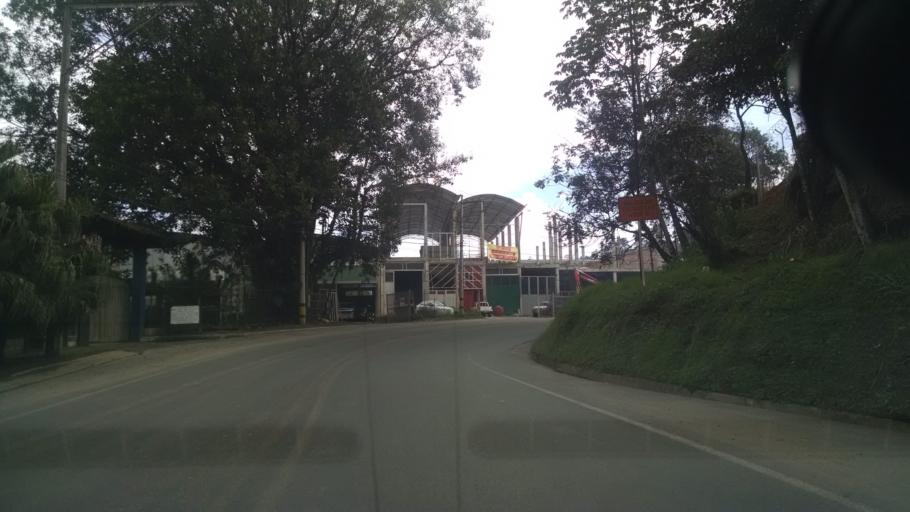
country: CO
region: Antioquia
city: Caldas
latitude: 6.0681
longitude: -75.6333
